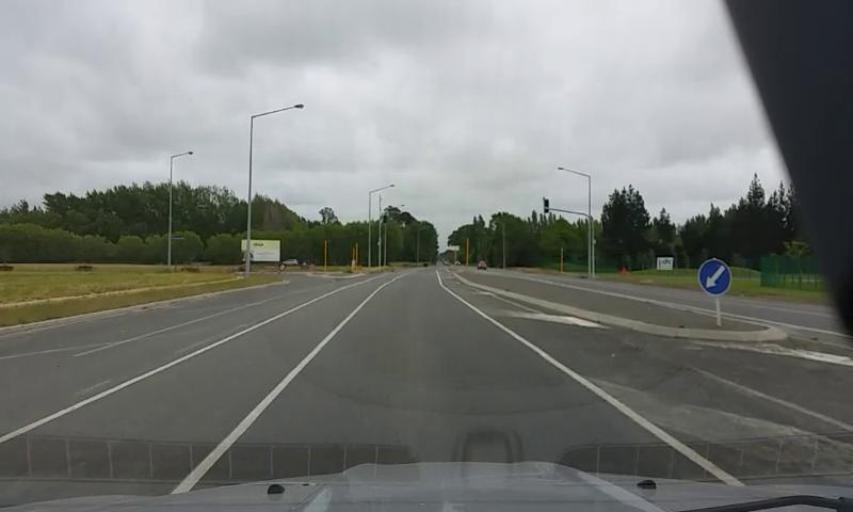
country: NZ
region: Canterbury
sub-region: Selwyn District
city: Prebbleton
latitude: -43.5184
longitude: 172.5275
